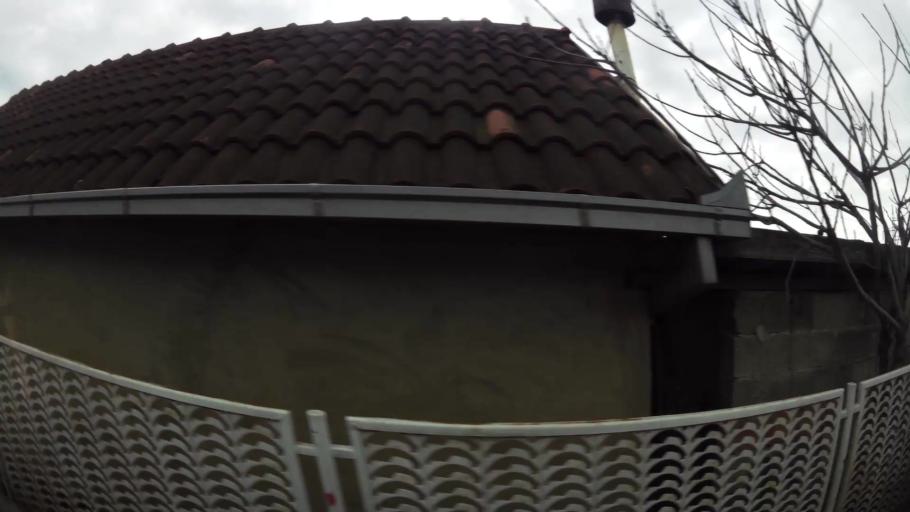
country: RS
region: Central Serbia
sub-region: Belgrade
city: Rakovica
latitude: 44.7433
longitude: 20.3998
